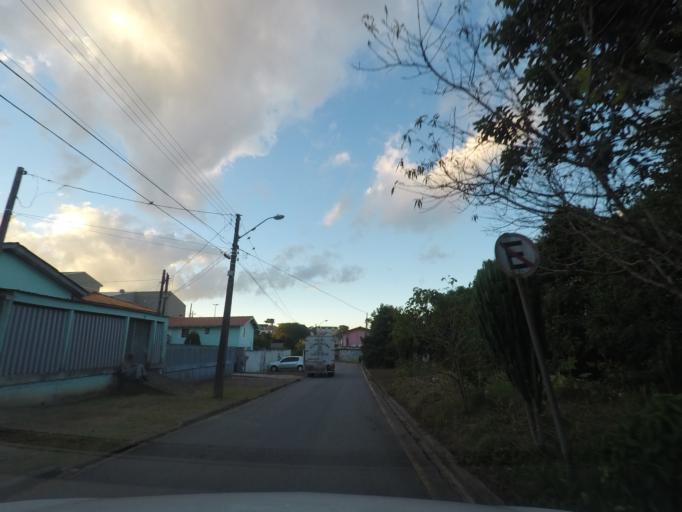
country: BR
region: Parana
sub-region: Sao Jose Dos Pinhais
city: Sao Jose dos Pinhais
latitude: -25.4998
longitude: -49.2591
